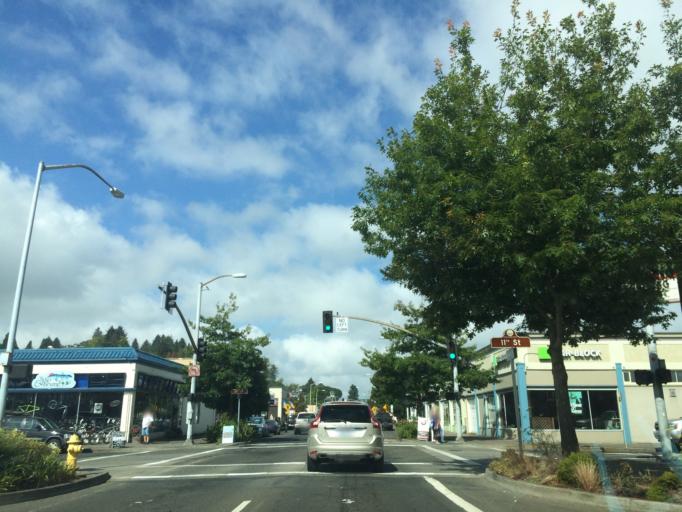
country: US
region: Oregon
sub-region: Clatsop County
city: Astoria
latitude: 46.1897
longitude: -123.8314
